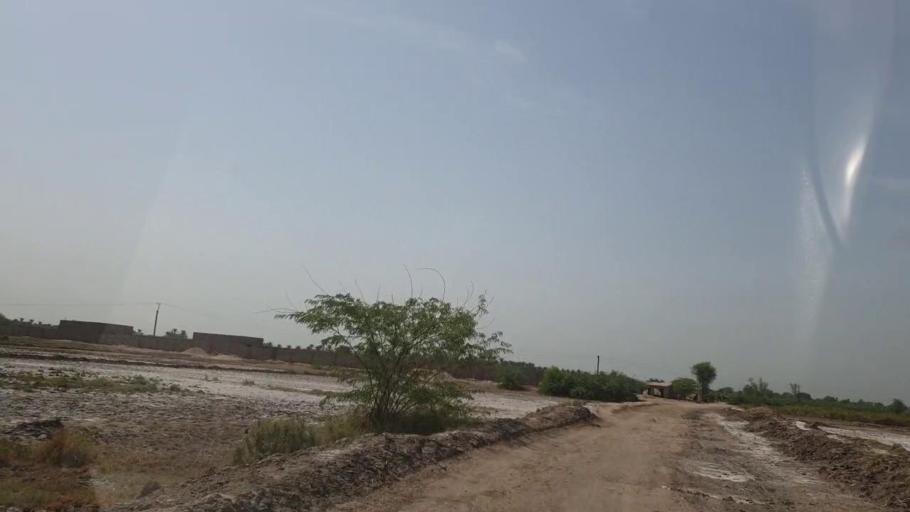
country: PK
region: Sindh
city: Gambat
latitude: 27.3796
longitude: 68.5833
